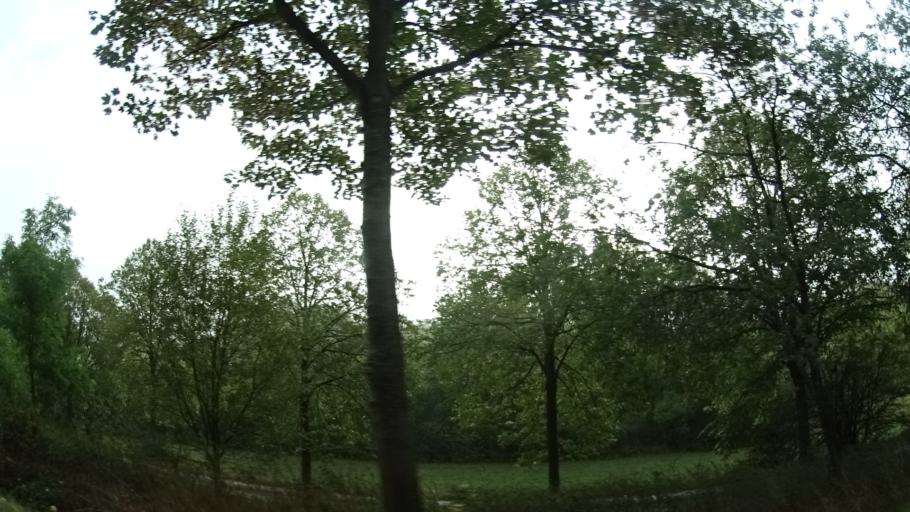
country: DE
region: Hesse
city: Gedern
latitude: 50.4334
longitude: 9.1999
